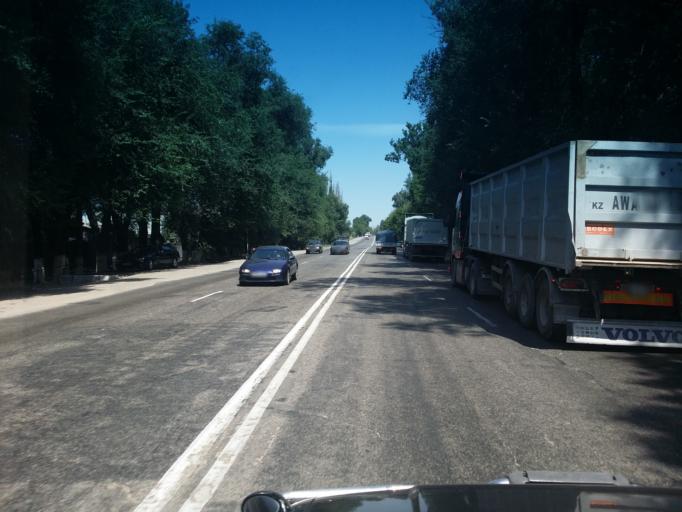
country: KZ
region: Almaty Oblysy
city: Energeticheskiy
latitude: 43.3409
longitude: 77.0457
